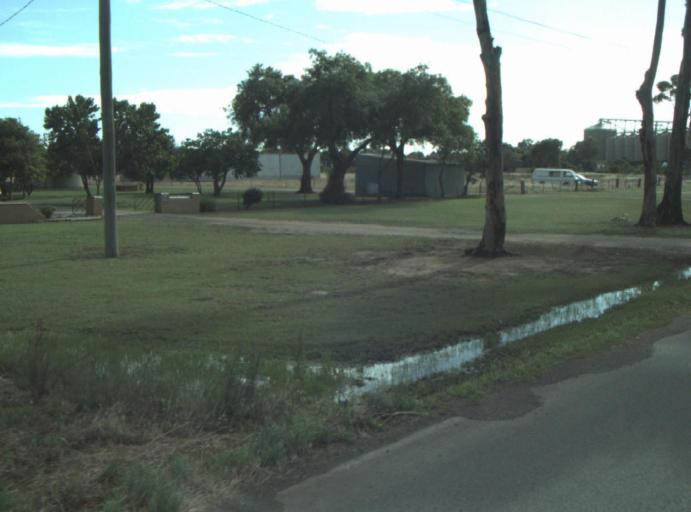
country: AU
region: Victoria
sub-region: Greater Geelong
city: Lara
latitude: -38.0266
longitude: 144.4309
